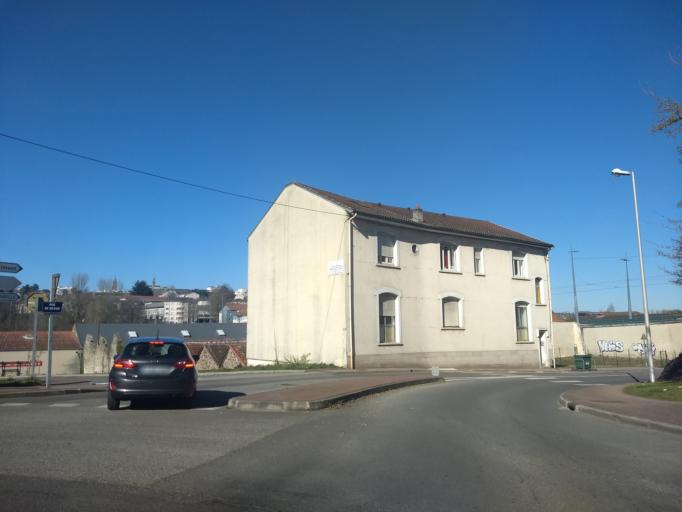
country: FR
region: Limousin
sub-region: Departement de la Haute-Vienne
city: Limoges
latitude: 45.8187
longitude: 1.2643
